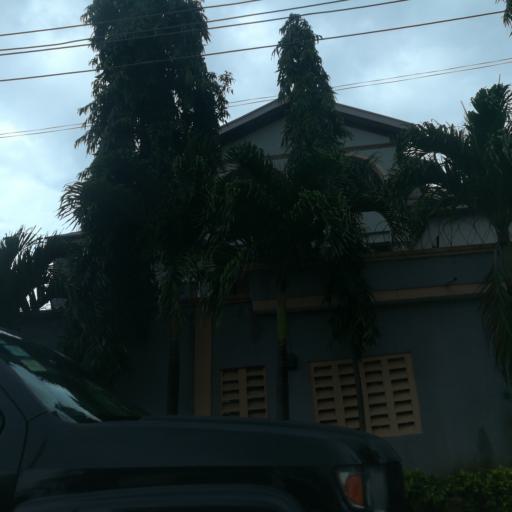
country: NG
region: Lagos
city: Ikoyi
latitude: 6.4397
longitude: 3.4621
